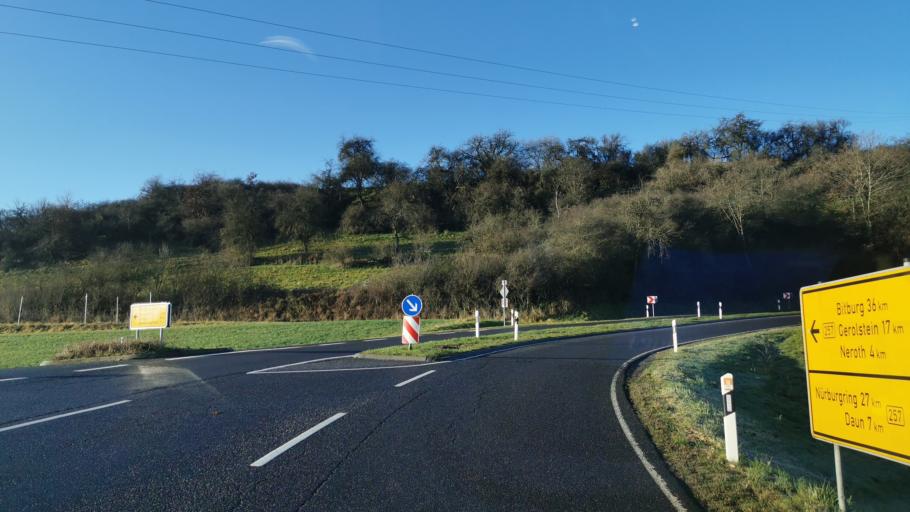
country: DE
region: Rheinland-Pfalz
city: Niederstadtfeld
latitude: 50.1730
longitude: 6.7683
